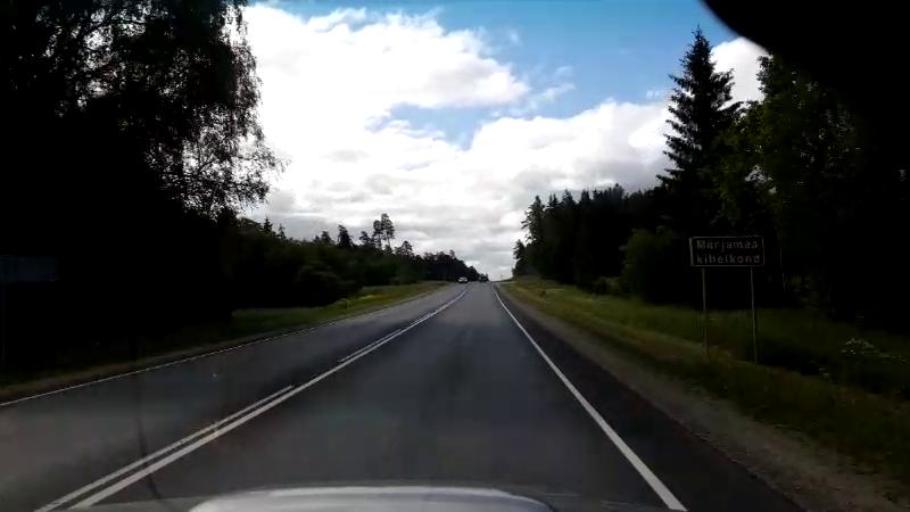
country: EE
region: Raplamaa
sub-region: Maerjamaa vald
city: Marjamaa
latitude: 59.0227
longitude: 24.4497
